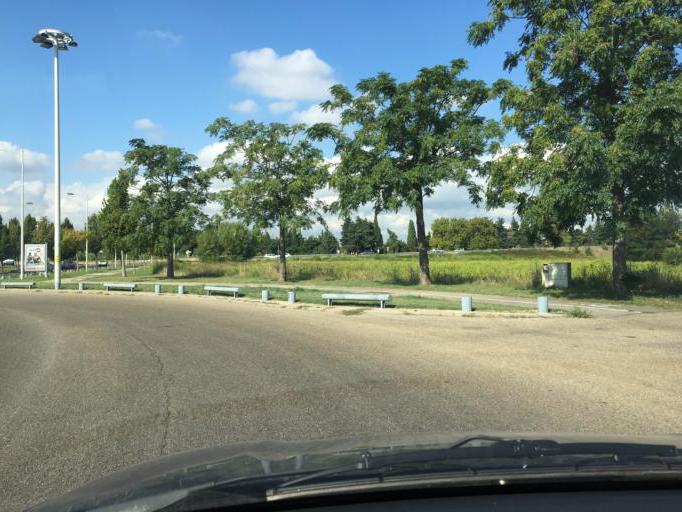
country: FR
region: Languedoc-Roussillon
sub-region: Departement du Gard
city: Nimes
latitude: 43.8102
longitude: 4.3567
